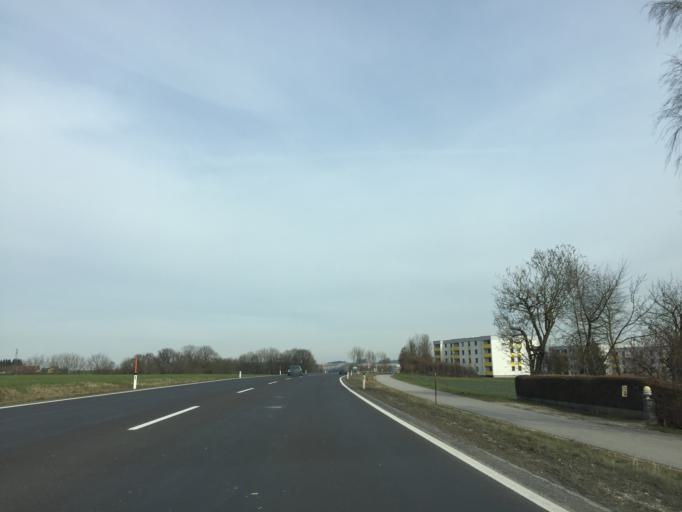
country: AT
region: Upper Austria
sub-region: Politischer Bezirk Ried im Innkreis
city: Ried im Innkreis
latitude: 48.2139
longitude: 13.4664
